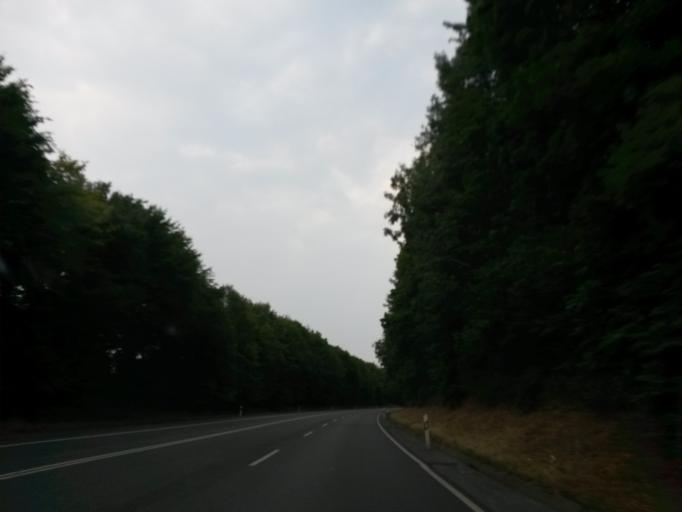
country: DE
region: North Rhine-Westphalia
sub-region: Regierungsbezirk Arnsberg
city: Hagen
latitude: 51.3452
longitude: 7.5155
